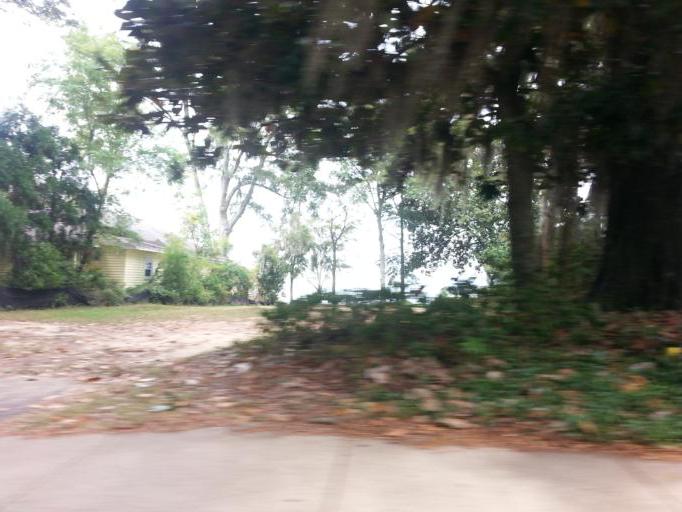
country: US
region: Alabama
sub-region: Baldwin County
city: Fairhope
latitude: 30.5196
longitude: -87.9137
